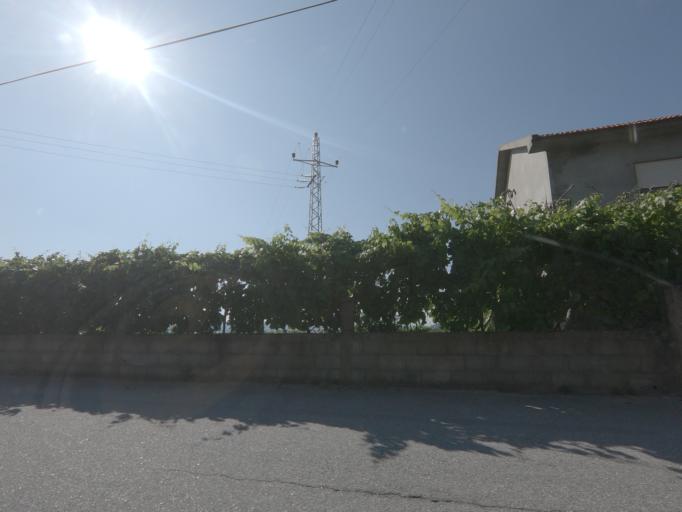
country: PT
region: Viseu
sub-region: Tabuaco
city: Tabuaco
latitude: 41.0471
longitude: -7.5689
